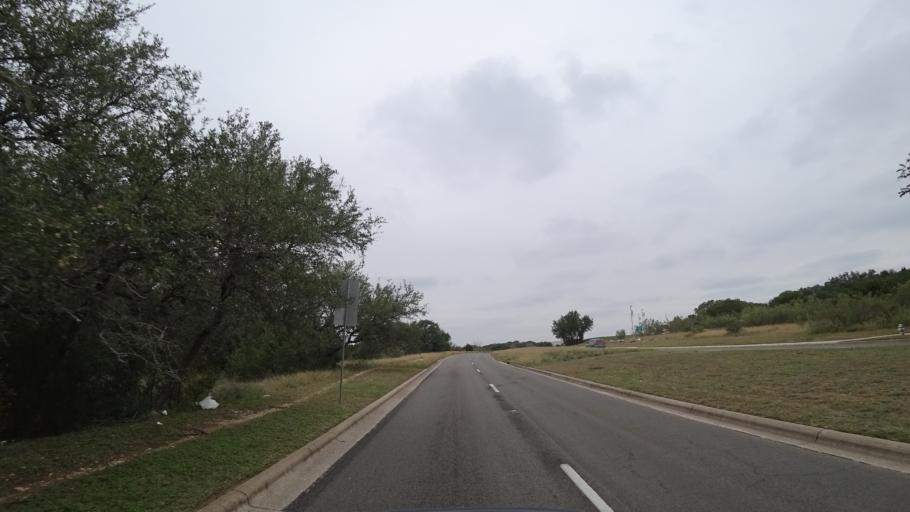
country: US
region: Texas
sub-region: Travis County
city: Shady Hollow
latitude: 30.2112
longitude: -97.8920
